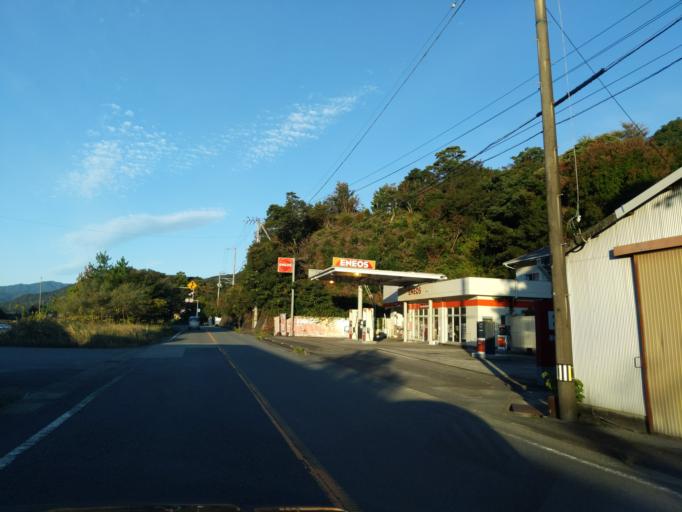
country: JP
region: Kochi
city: Muroto-misakicho
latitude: 33.5854
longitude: 134.3449
